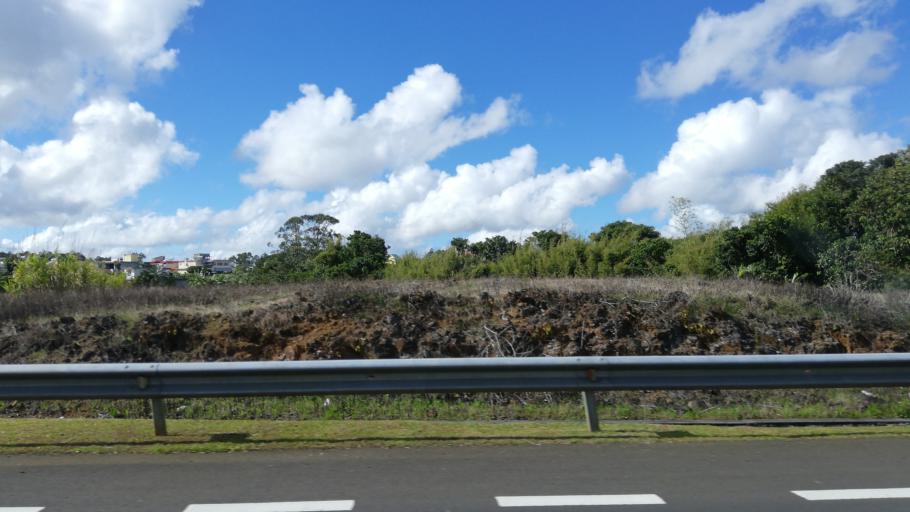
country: MU
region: Moka
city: La Dagotiere
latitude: -20.2530
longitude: 57.5651
